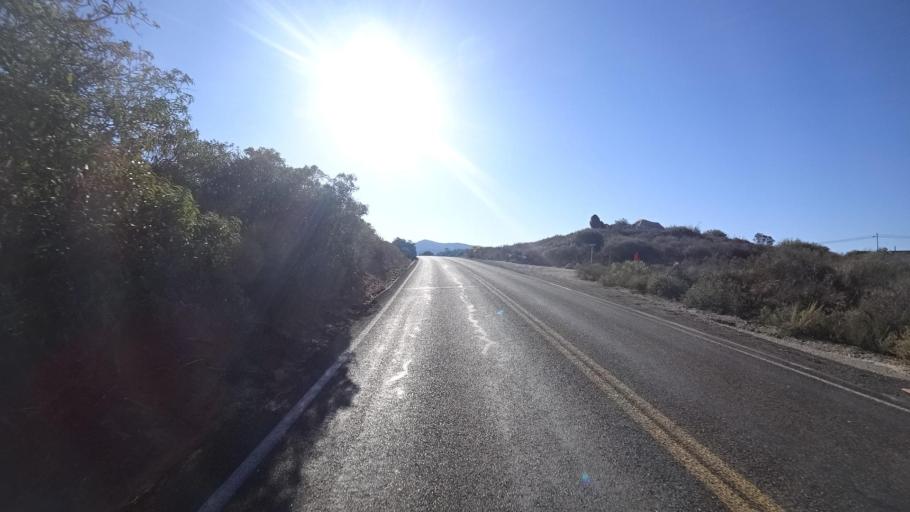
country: MX
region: Baja California
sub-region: Tijuana
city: Villa del Campo
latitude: 32.6221
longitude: -116.7475
